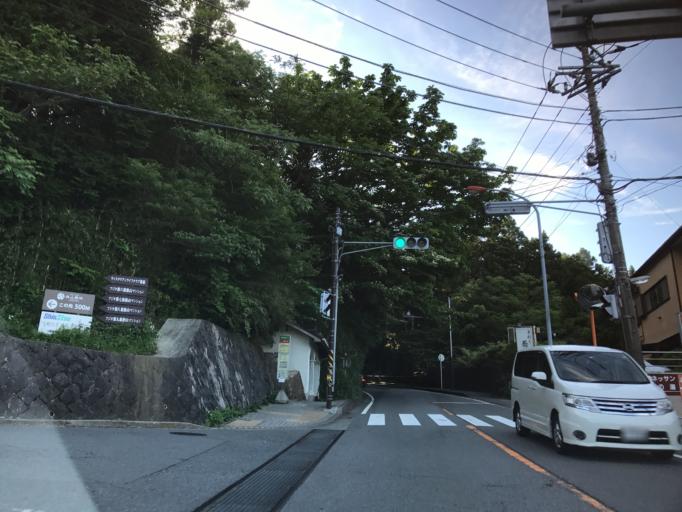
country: JP
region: Kanagawa
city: Hakone
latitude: 35.2408
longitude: 139.0494
